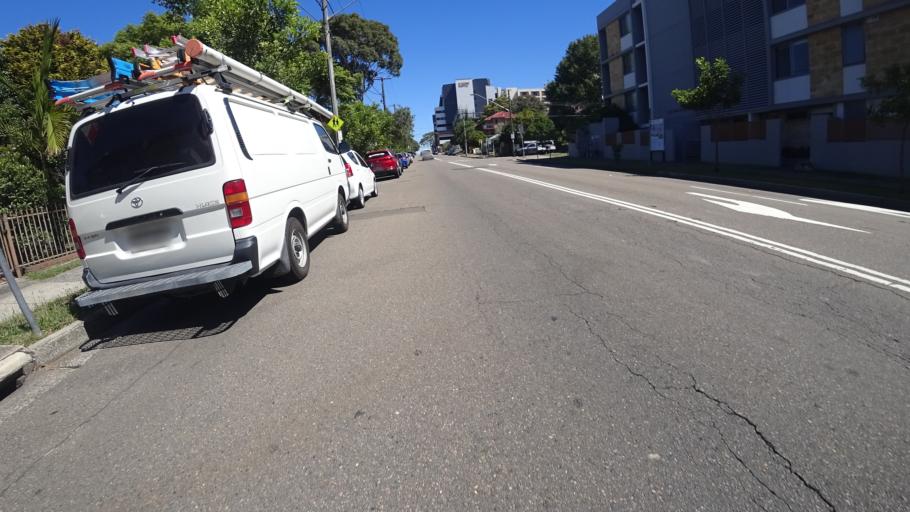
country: AU
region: New South Wales
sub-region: Kogarah
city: Beverly Park
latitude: -33.9696
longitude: 151.1346
